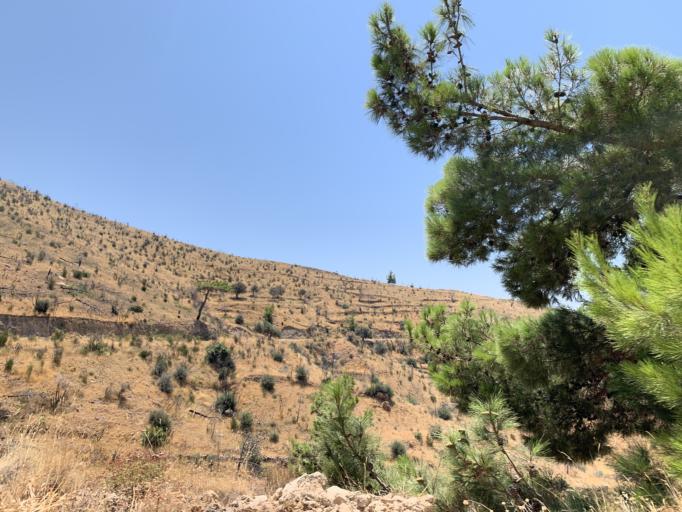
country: GR
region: North Aegean
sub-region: Chios
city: Vrontados
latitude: 38.4433
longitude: 25.9769
